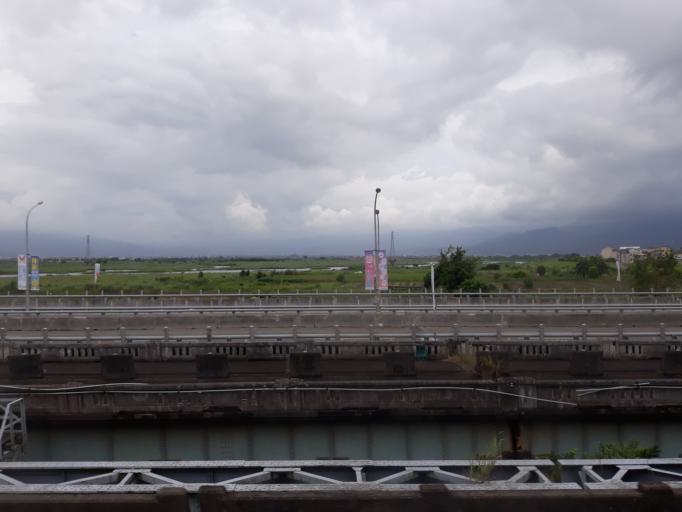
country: TW
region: Taiwan
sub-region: Yilan
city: Yilan
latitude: 24.7177
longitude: 121.7717
